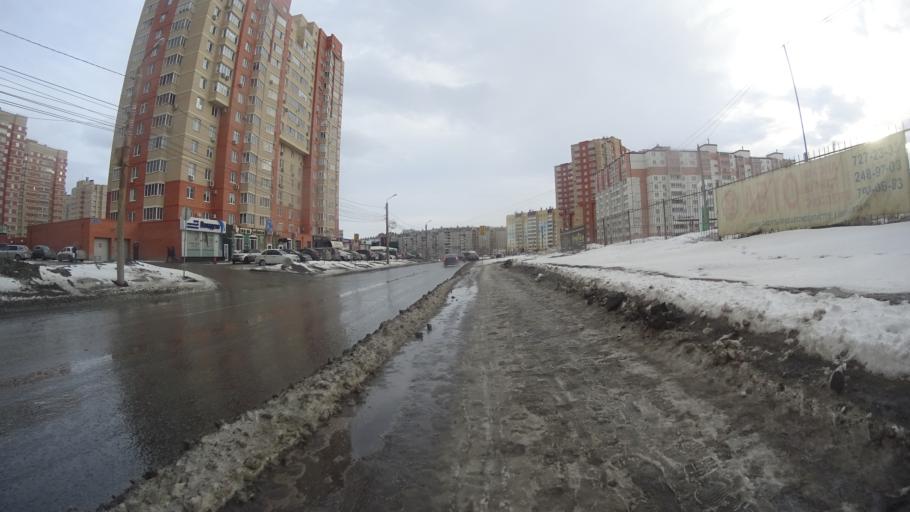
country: RU
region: Chelyabinsk
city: Roshchino
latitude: 55.1940
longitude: 61.2802
